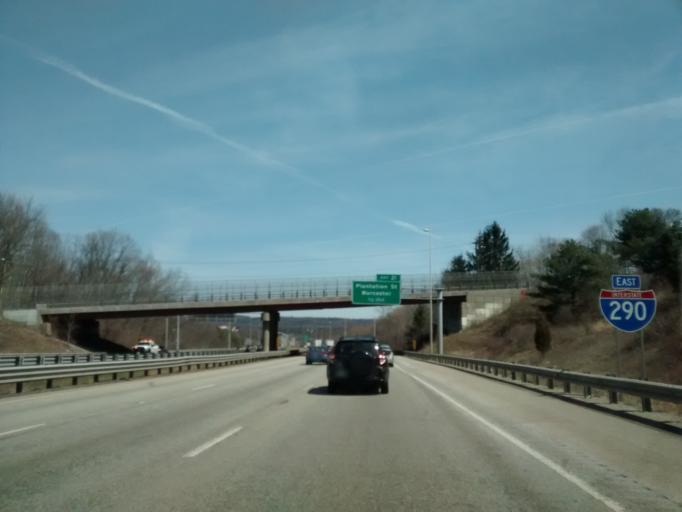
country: US
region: Massachusetts
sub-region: Worcester County
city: Worcester
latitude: 42.2901
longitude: -71.7799
